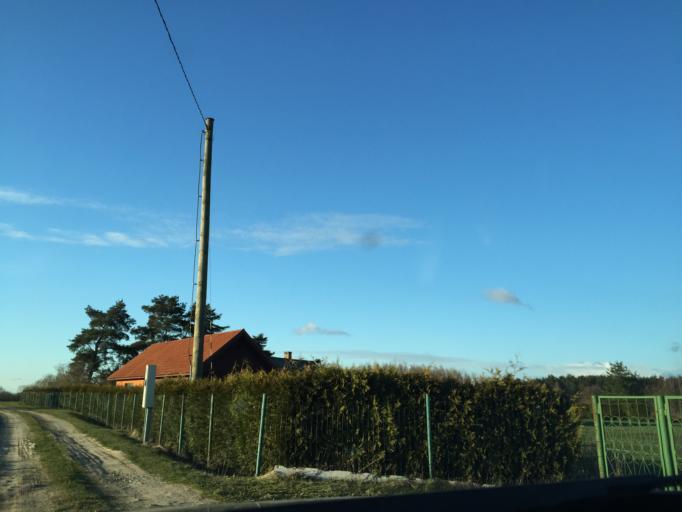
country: LV
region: Kekava
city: Kekava
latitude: 56.8683
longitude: 24.1994
